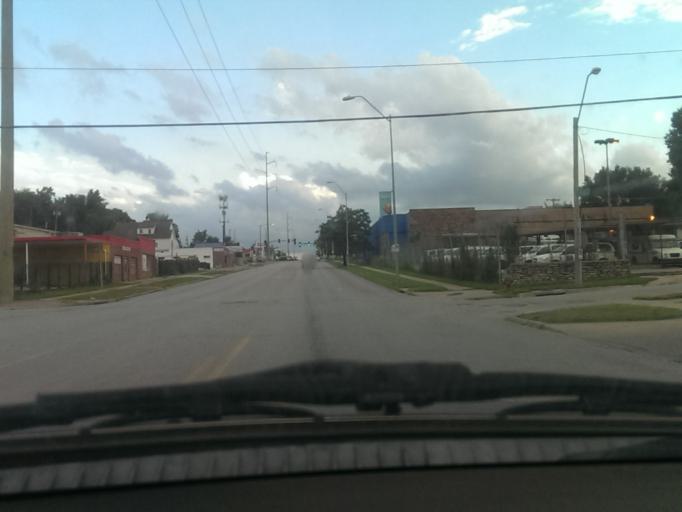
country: US
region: Kansas
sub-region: Johnson County
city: Mission Hills
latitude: 38.9937
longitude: -94.5756
